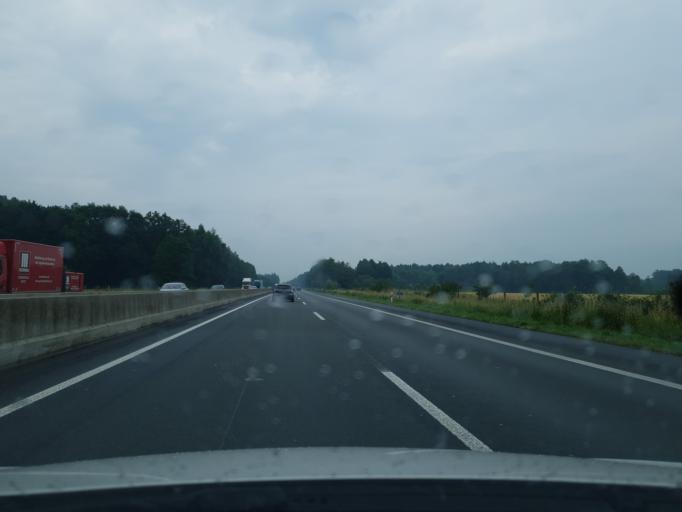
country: DE
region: North Rhine-Westphalia
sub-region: Regierungsbezirk Munster
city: Gescher
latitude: 51.9705
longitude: 7.0479
